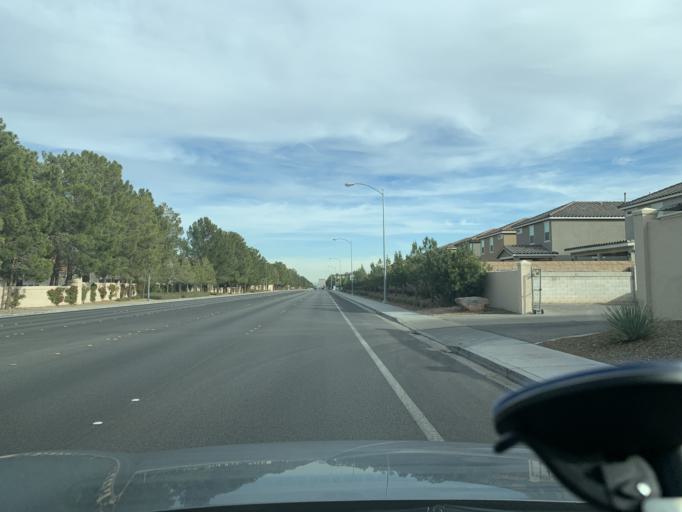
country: US
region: Nevada
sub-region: Clark County
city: Spring Valley
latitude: 36.0923
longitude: -115.2512
